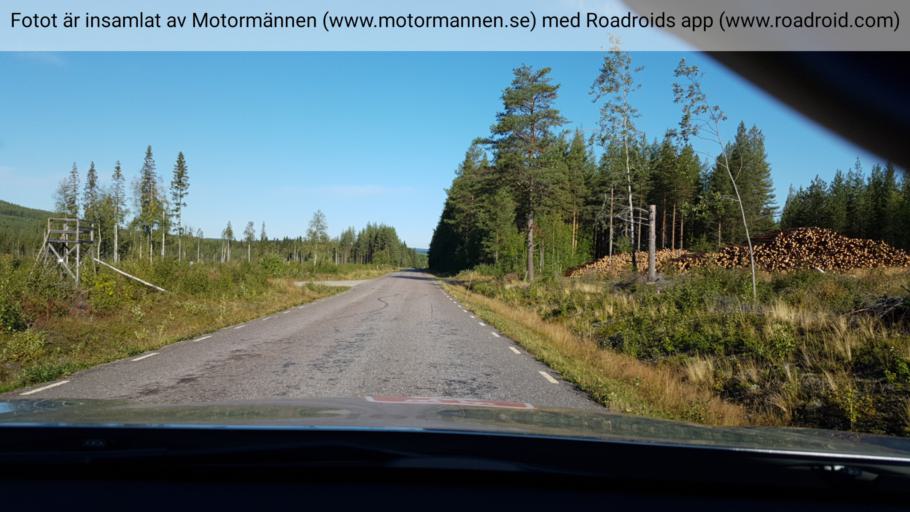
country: SE
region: Vaesterbotten
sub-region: Lycksele Kommun
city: Lycksele
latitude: 64.5113
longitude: 18.7767
